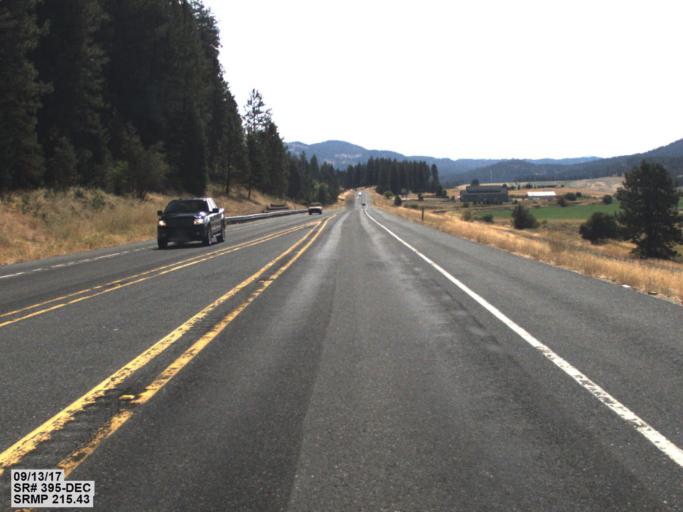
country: US
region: Washington
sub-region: Stevens County
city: Chewelah
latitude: 48.3515
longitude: -117.8337
